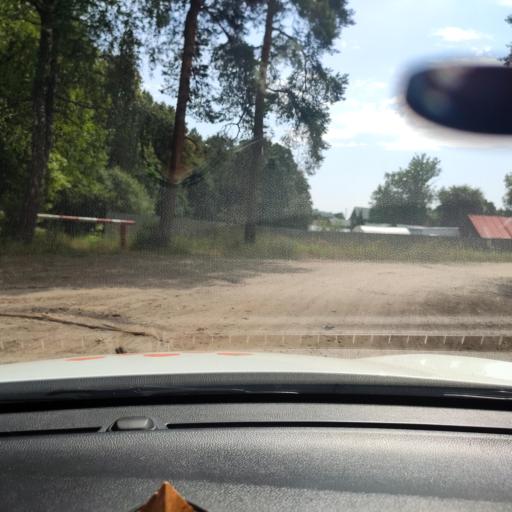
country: RU
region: Tatarstan
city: Osinovo
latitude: 55.9111
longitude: 48.9628
